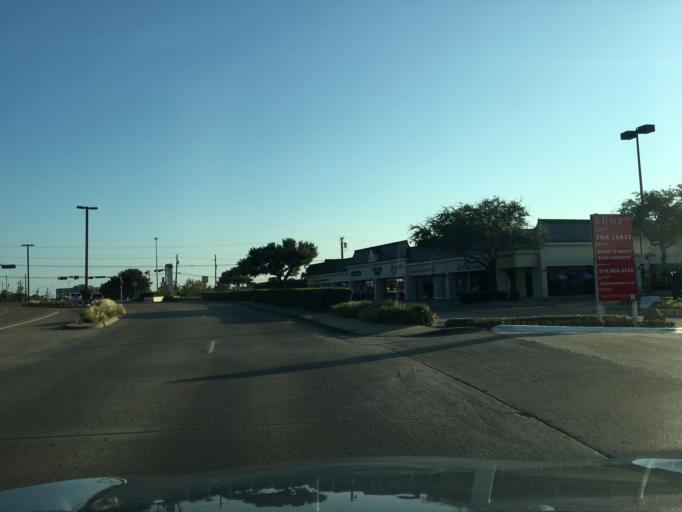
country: US
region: Texas
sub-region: Dallas County
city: Addison
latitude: 32.9528
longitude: -96.8184
